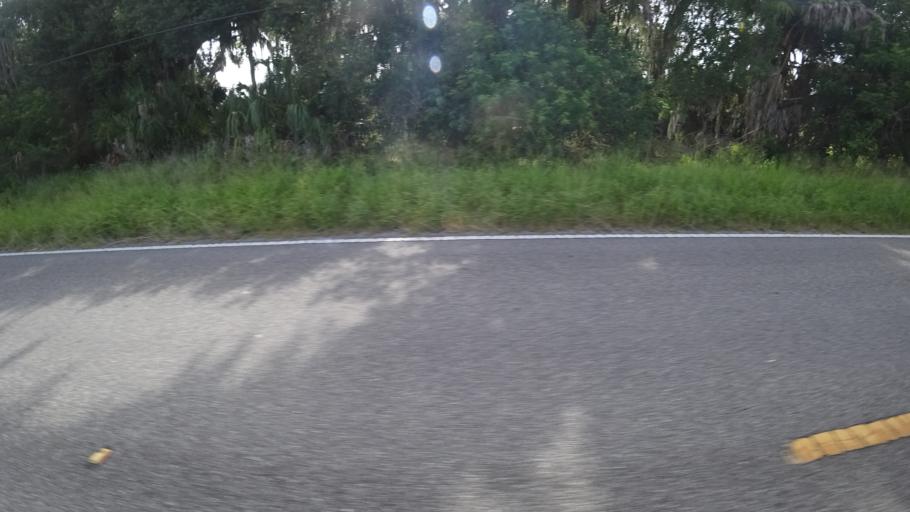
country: US
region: Florida
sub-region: Manatee County
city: Ellenton
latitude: 27.5366
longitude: -82.5283
